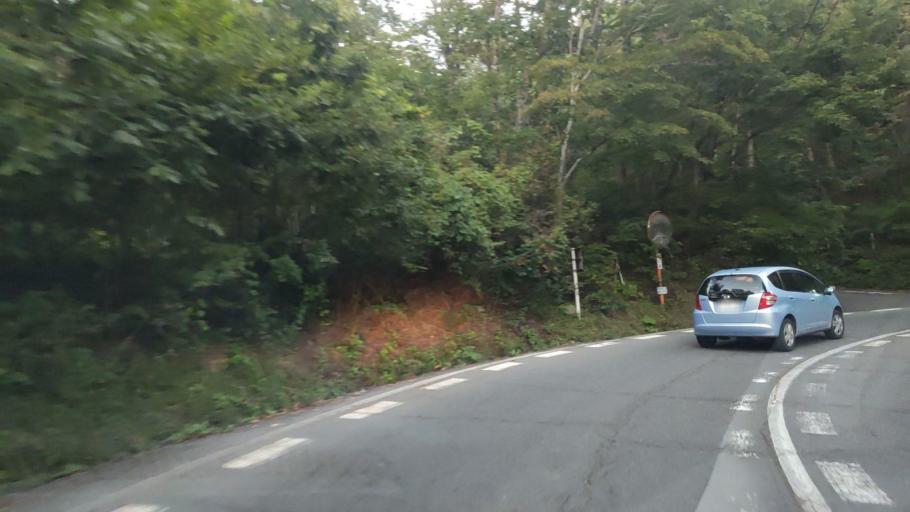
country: JP
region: Nagano
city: Komoro
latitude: 36.3800
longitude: 138.5844
